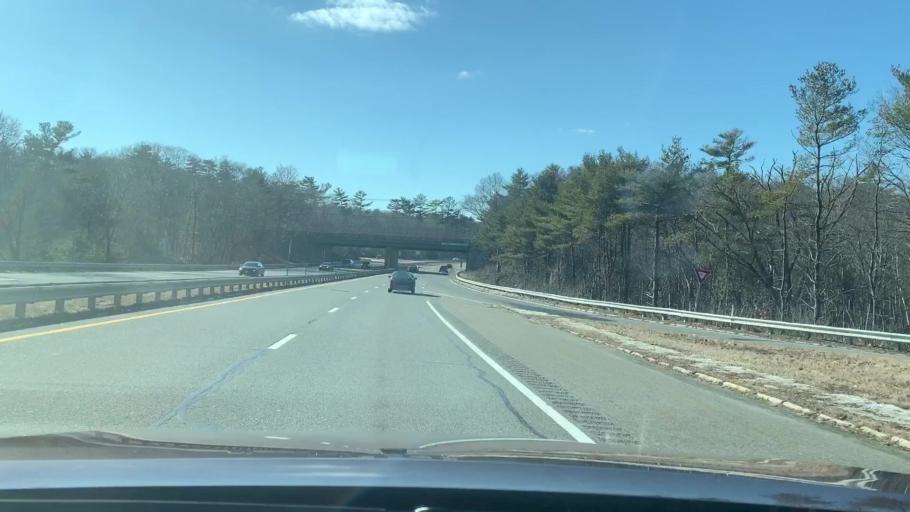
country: US
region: Massachusetts
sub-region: Essex County
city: Essex
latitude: 42.5903
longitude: -70.7633
